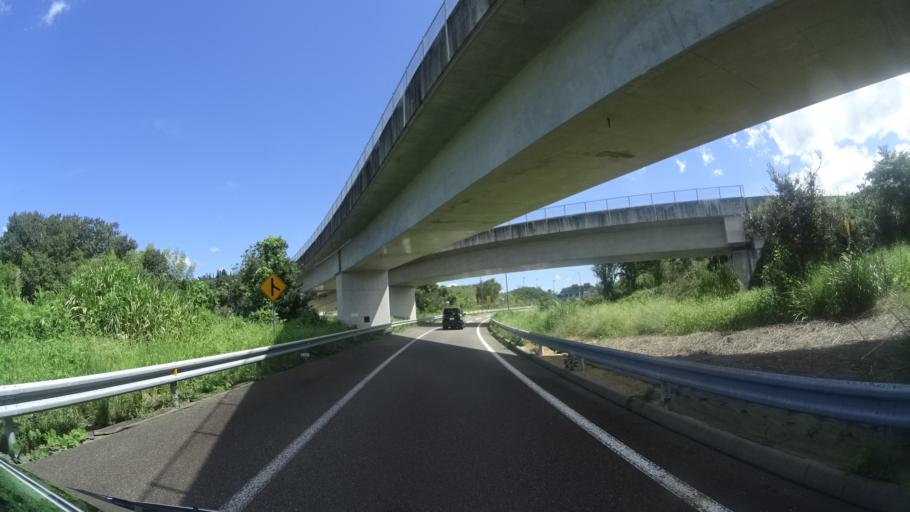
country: JP
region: Gifu
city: Minokamo
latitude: 35.4714
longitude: 137.0220
